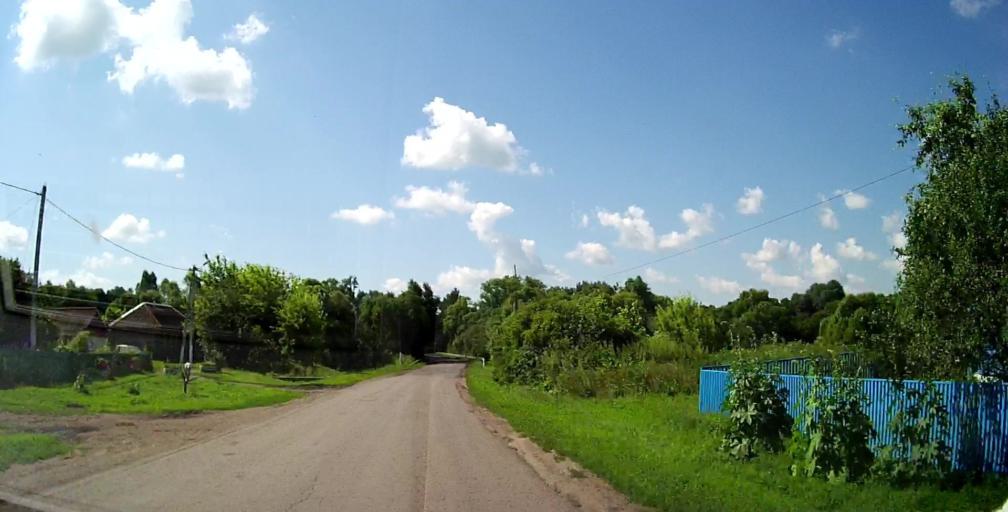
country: RU
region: Lipetsk
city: Chaplygin
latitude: 53.3722
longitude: 39.9167
